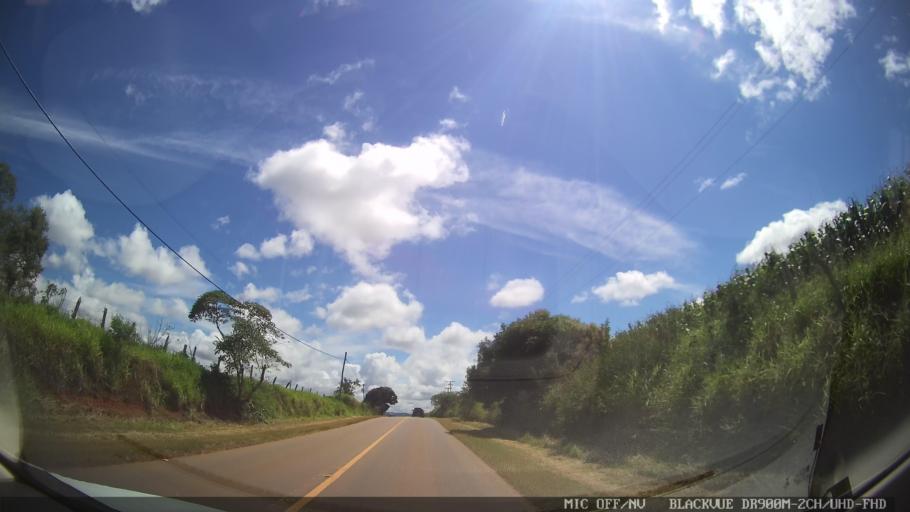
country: BR
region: Sao Paulo
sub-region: Amparo
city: Amparo
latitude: -22.8370
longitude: -46.7052
